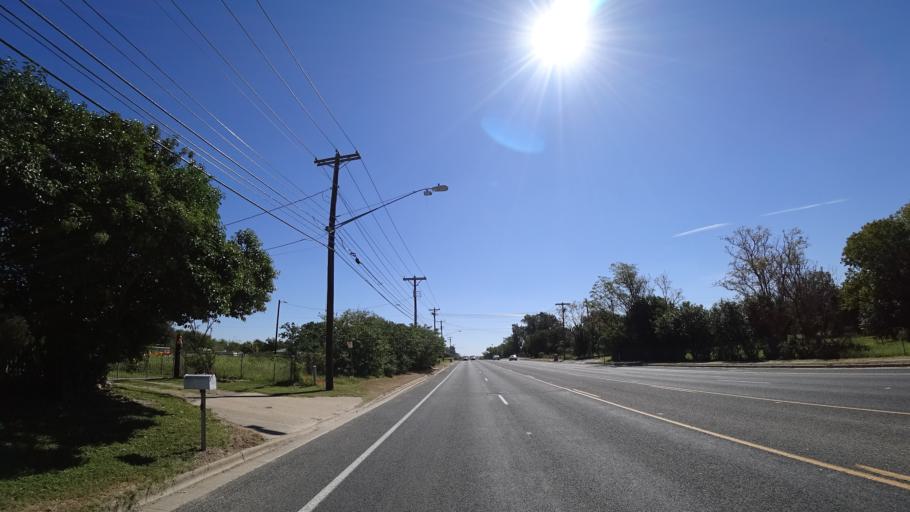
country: US
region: Texas
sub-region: Travis County
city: Austin
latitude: 30.1888
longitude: -97.6950
